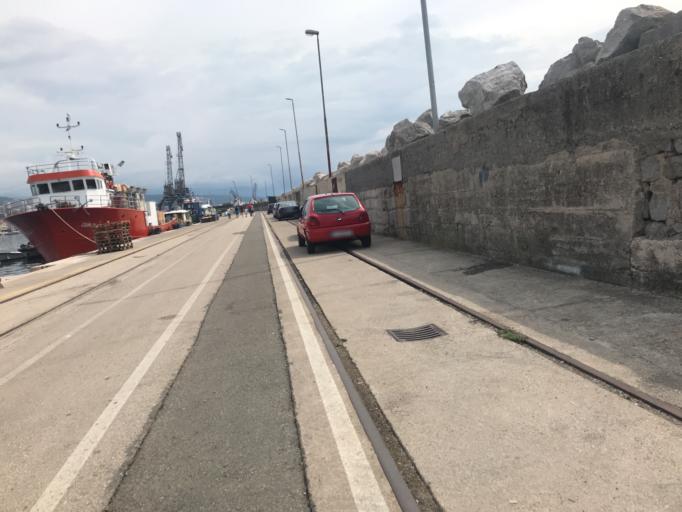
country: HR
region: Primorsko-Goranska
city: Drenova
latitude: 45.3252
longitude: 14.4299
